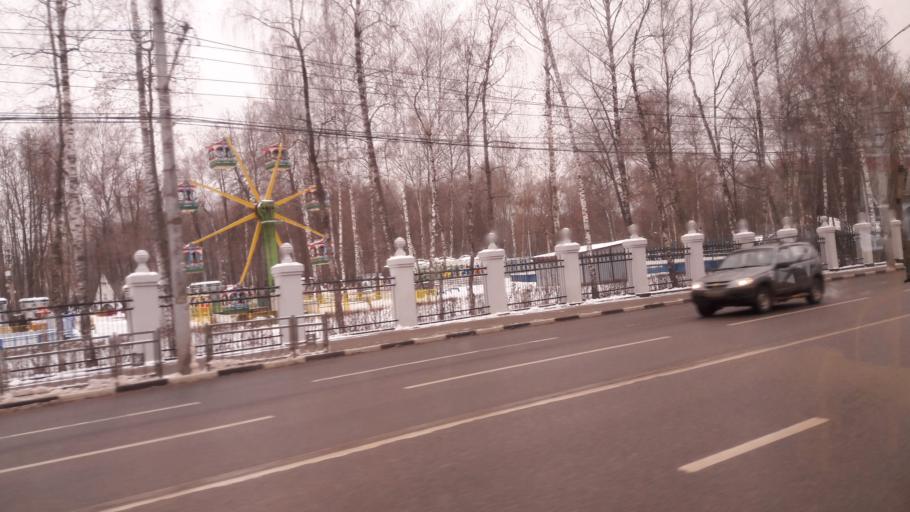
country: RU
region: Tula
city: Gorelki
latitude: 54.2281
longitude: 37.6282
